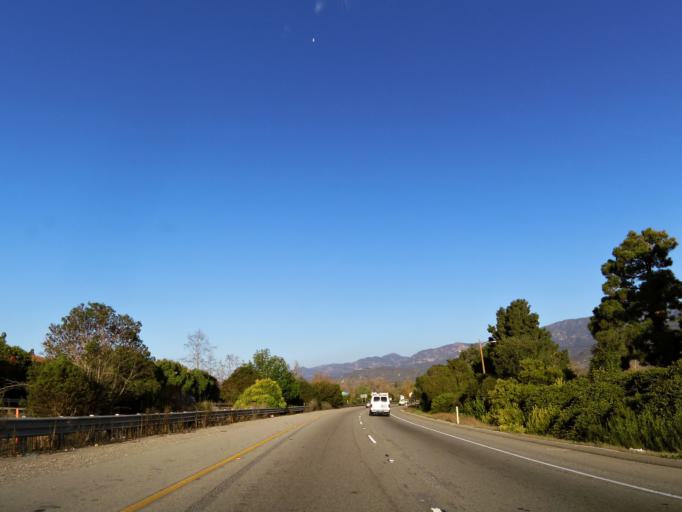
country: US
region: California
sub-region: Santa Barbara County
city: Carpinteria
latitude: 34.3917
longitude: -119.5074
